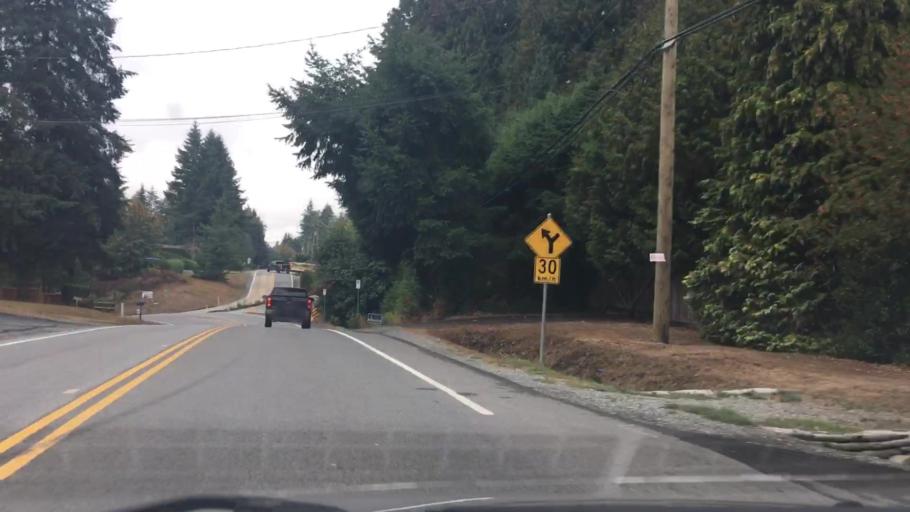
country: CA
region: British Columbia
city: Langley
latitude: 49.1041
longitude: -122.5423
